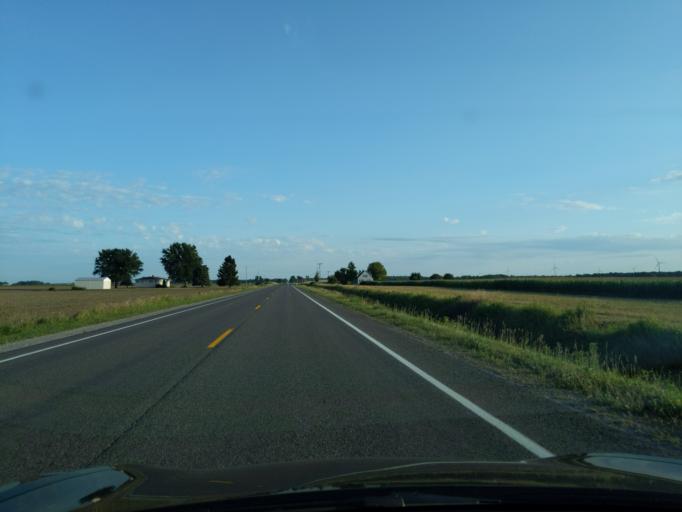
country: US
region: Michigan
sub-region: Gratiot County
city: Breckenridge
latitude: 43.4870
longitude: -84.3698
